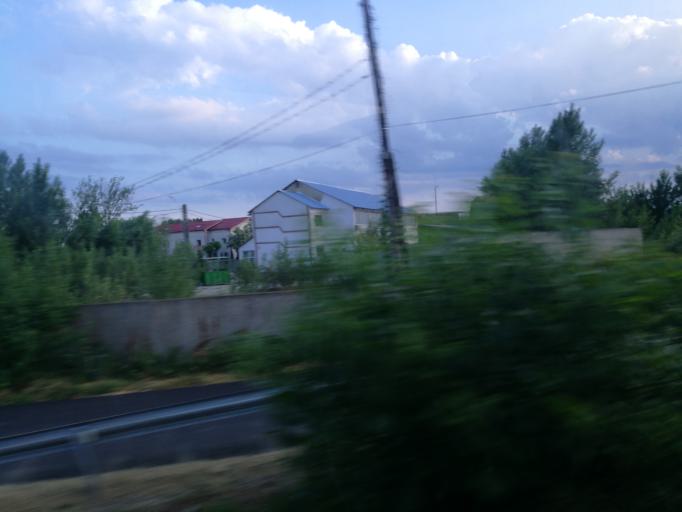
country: RO
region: Dambovita
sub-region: Comuna Branistea
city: Dambovicioara
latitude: 44.6623
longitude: 25.5609
